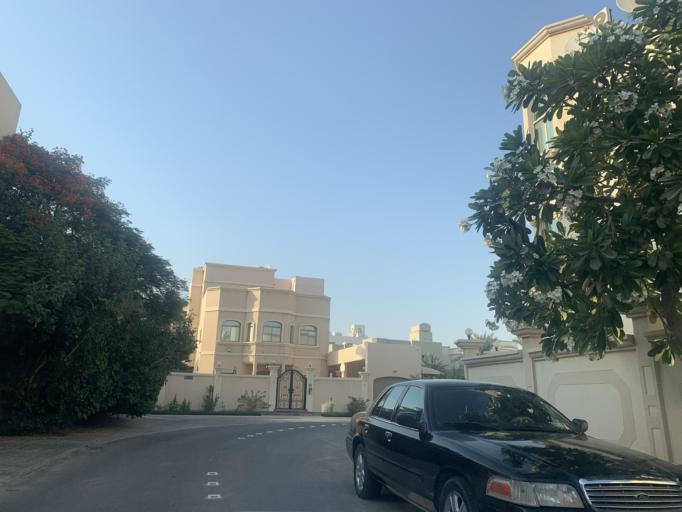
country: BH
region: Manama
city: Jidd Hafs
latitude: 26.2155
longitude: 50.5269
